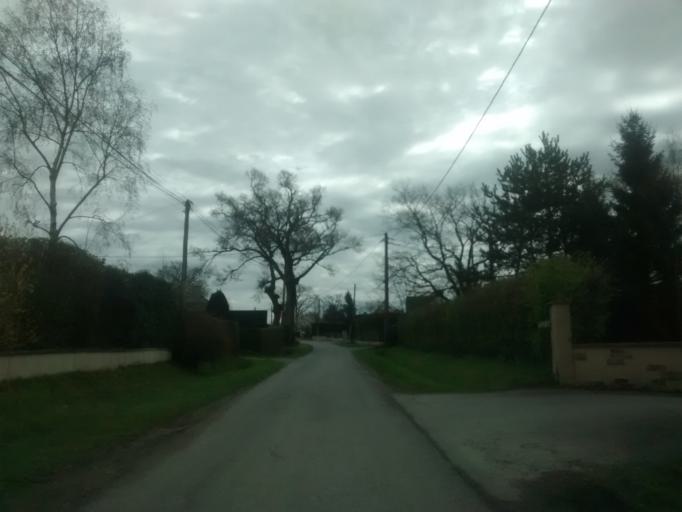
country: FR
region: Brittany
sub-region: Departement d'Ille-et-Vilaine
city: Chasne-sur-Illet
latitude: 48.2477
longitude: -1.5423
